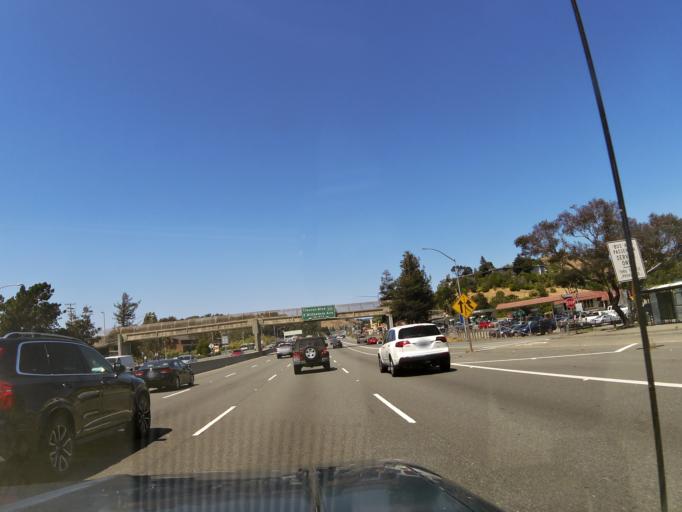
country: US
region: California
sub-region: Marin County
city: Strawberry
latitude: 37.8882
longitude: -122.5166
